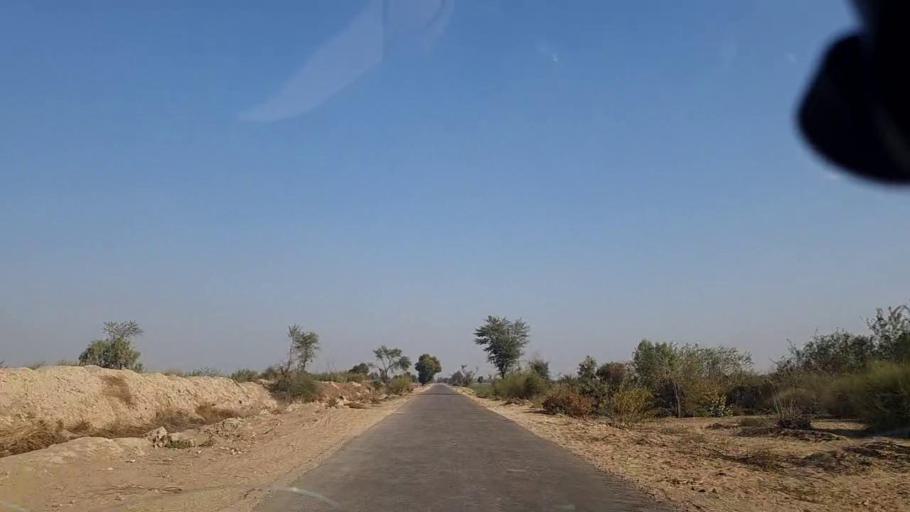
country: PK
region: Sindh
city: Khanpur
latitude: 27.6823
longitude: 69.5359
